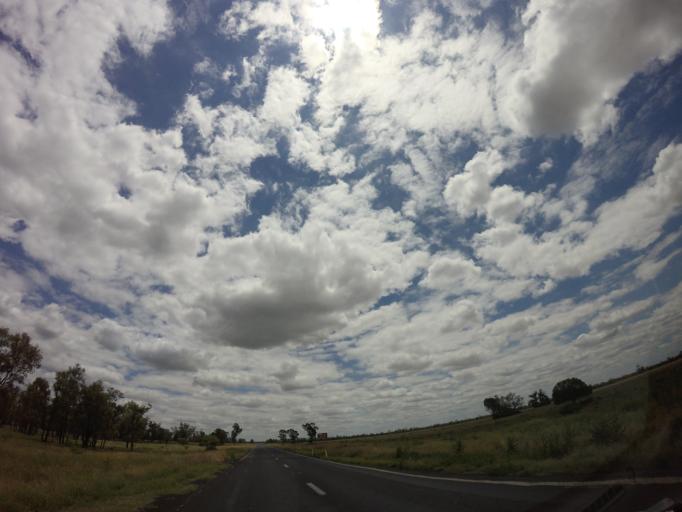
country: AU
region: New South Wales
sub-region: Moree Plains
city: Boggabilla
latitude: -28.6371
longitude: 150.3439
